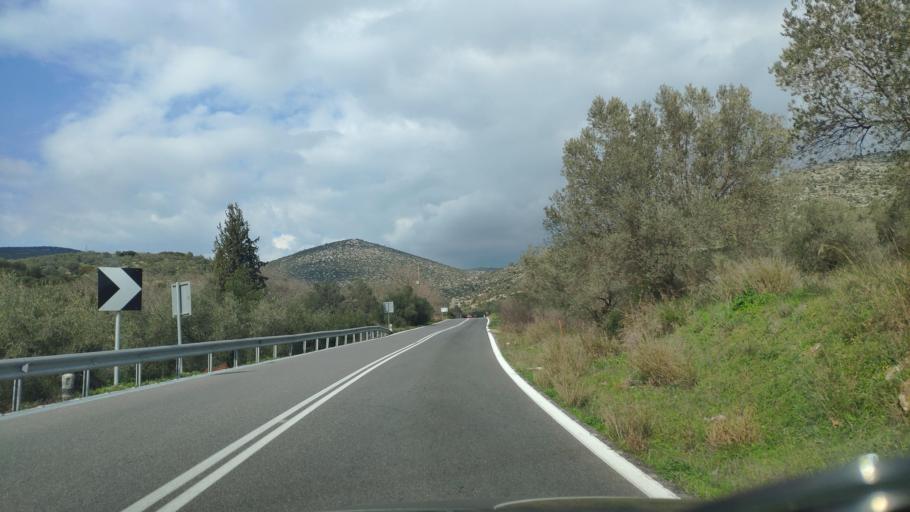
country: GR
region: Peloponnese
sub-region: Nomos Korinthias
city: Ayios Vasilios
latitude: 37.7751
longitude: 22.7253
